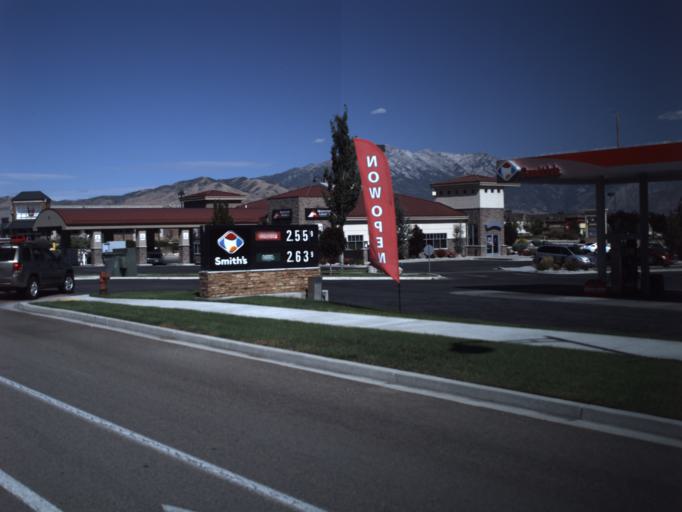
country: US
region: Utah
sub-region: Utah County
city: Saratoga Springs
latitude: 40.3864
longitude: -111.9162
